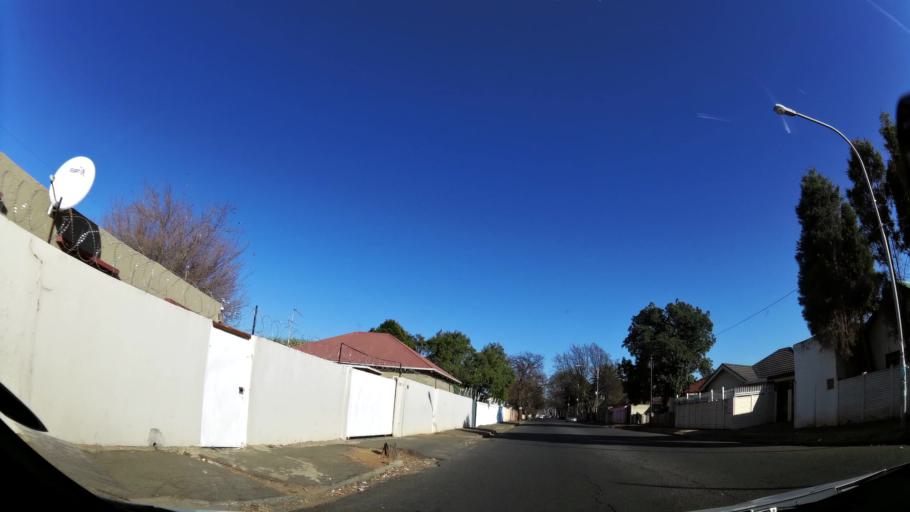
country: ZA
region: Gauteng
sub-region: Ekurhuleni Metropolitan Municipality
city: Germiston
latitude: -26.1981
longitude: 28.1199
